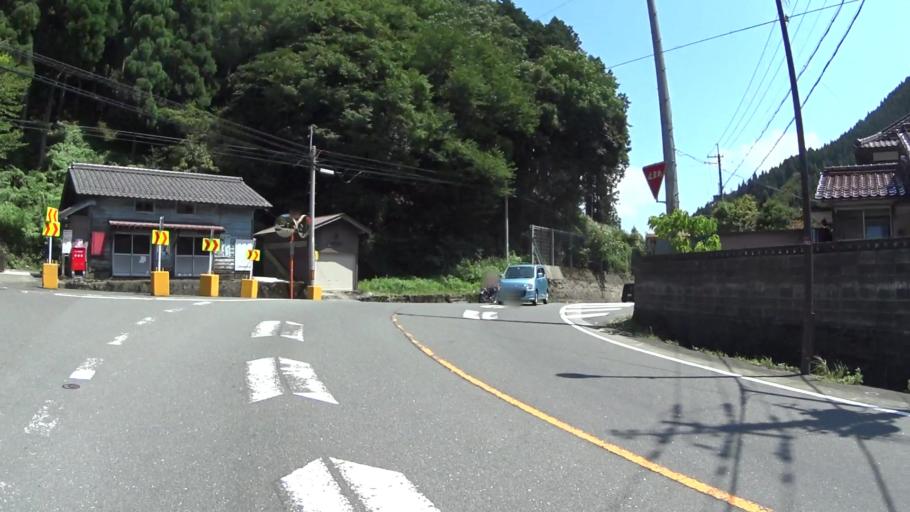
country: JP
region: Fukui
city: Obama
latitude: 35.4143
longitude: 135.9426
